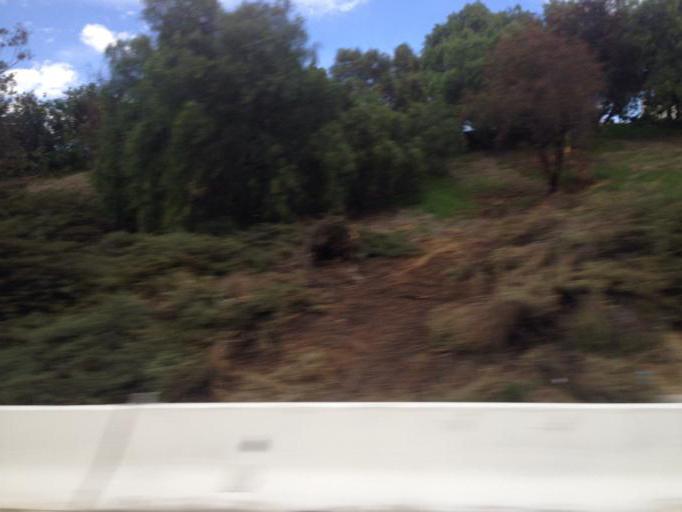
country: US
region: California
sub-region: San Diego County
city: National City
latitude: 32.6737
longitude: -117.0827
